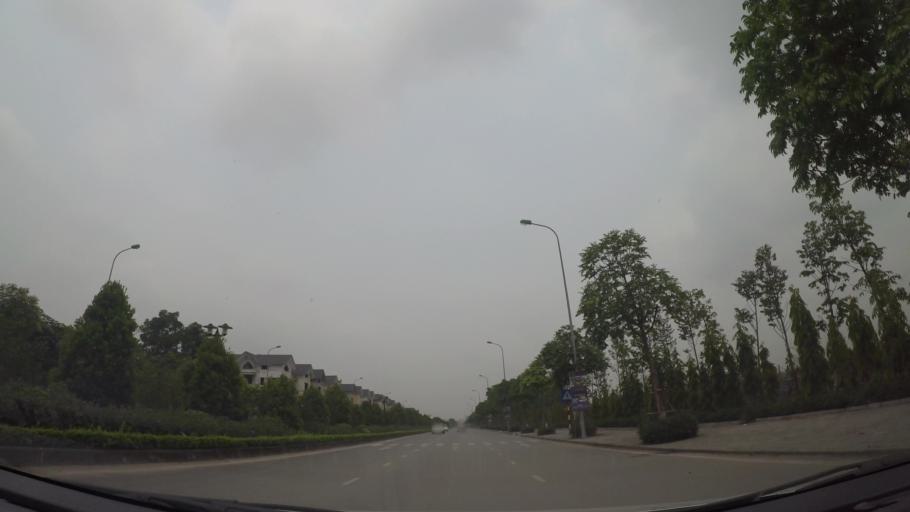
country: VN
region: Ha Noi
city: Ha Dong
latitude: 20.9788
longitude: 105.7629
